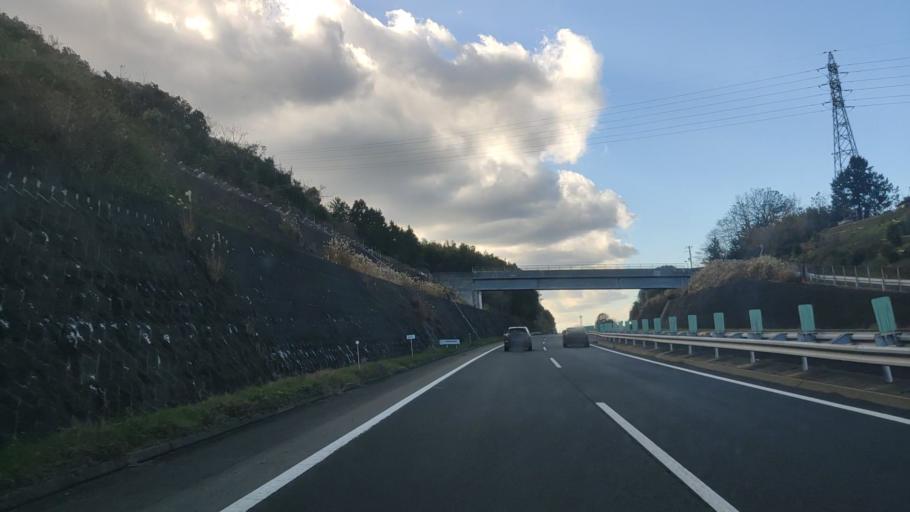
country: JP
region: Ehime
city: Kawanoecho
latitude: 33.9699
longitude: 133.5525
